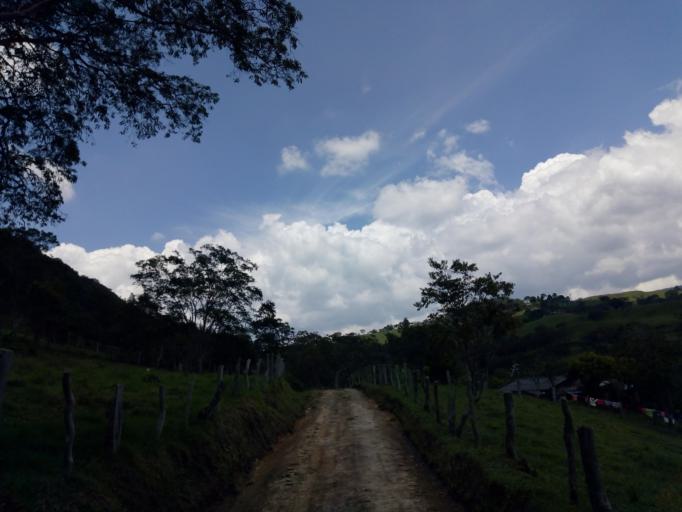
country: CO
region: Boyaca
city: Moniquira
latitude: 5.8668
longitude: -73.5147
